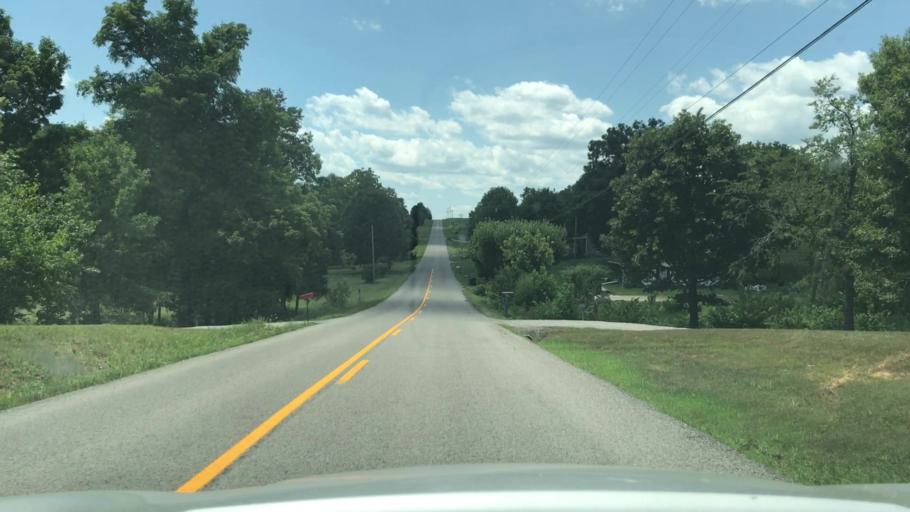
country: US
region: Kentucky
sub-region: Christian County
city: Hopkinsville
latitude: 36.9712
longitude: -87.3729
